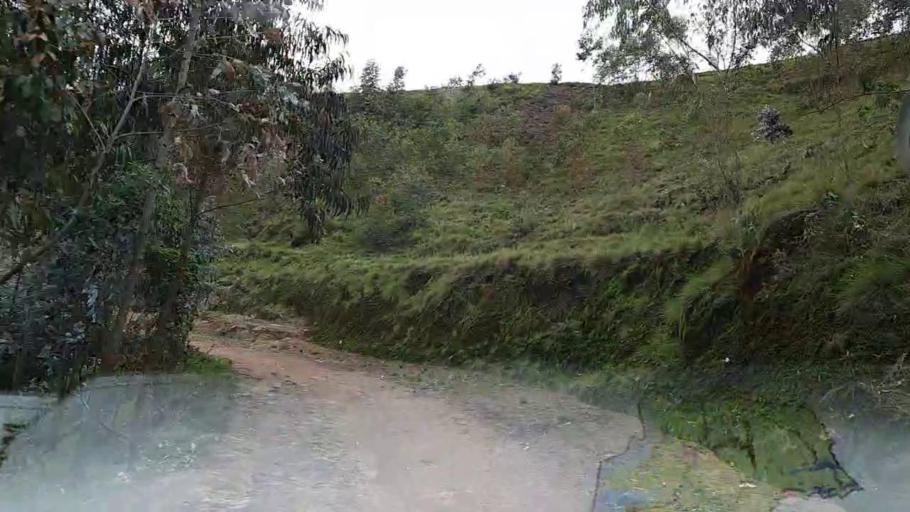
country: RW
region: Southern Province
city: Nzega
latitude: -2.4092
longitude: 29.4926
